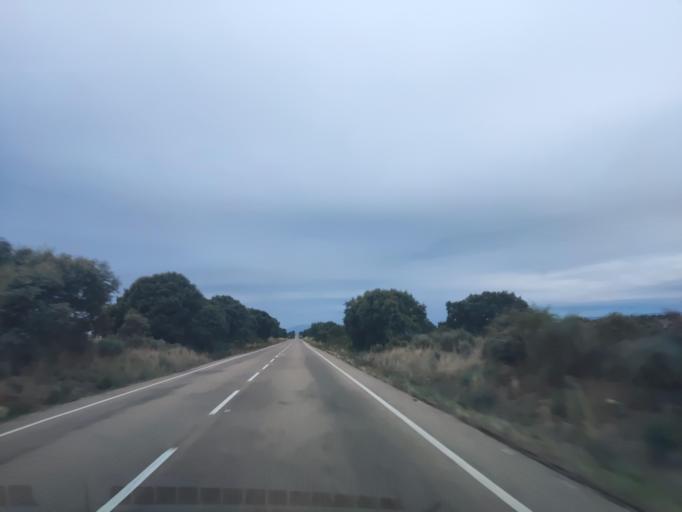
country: ES
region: Castille and Leon
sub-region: Provincia de Salamanca
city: Hinojosa de Duero
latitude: 40.9597
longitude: -6.7957
